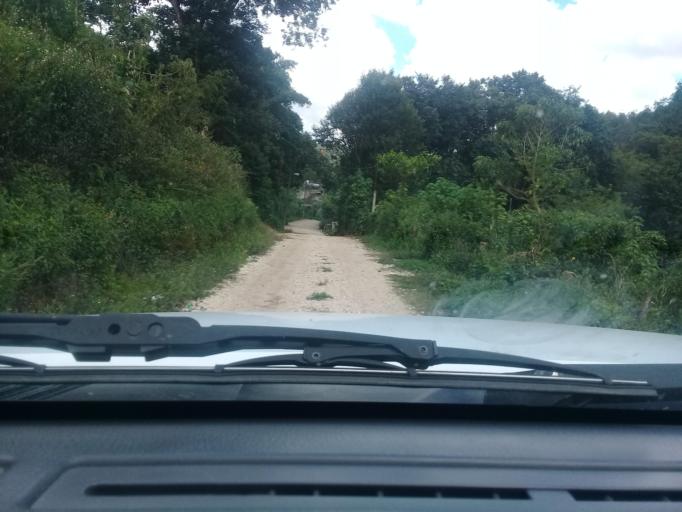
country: MX
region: Veracruz
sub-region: Tlalnelhuayocan
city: Otilpan
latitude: 19.5401
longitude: -96.9781
